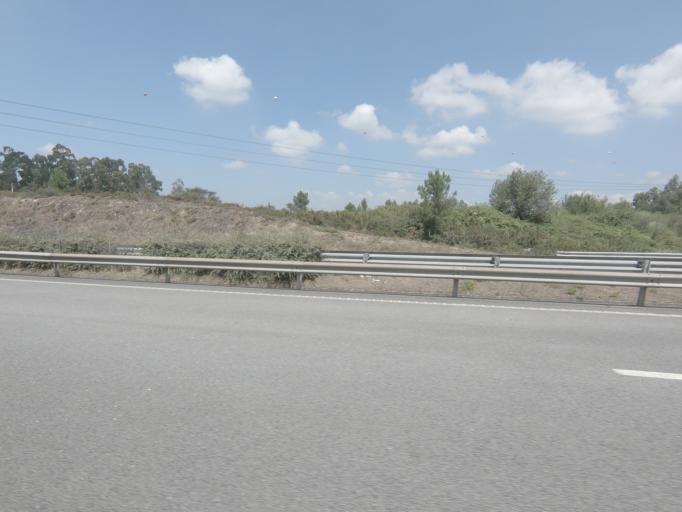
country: PT
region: Porto
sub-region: Paredes
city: Recarei
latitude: 41.1726
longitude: -8.4282
